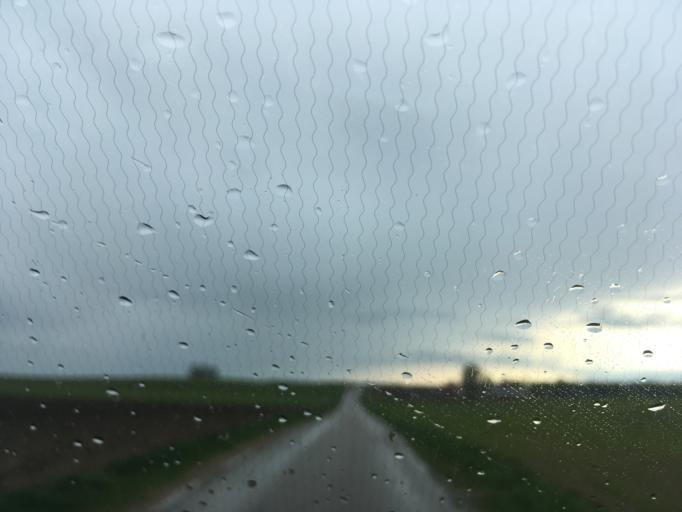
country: PL
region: Warmian-Masurian Voivodeship
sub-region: Powiat dzialdowski
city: Rybno
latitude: 53.3840
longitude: 19.9738
